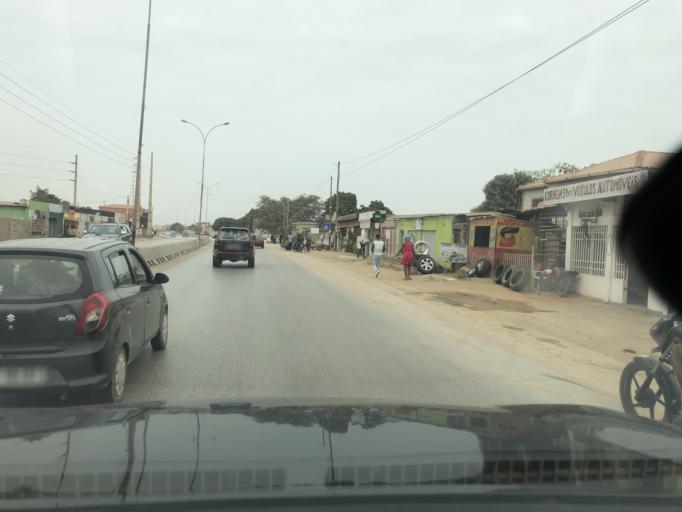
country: AO
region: Luanda
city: Luanda
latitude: -8.9019
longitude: 13.2510
